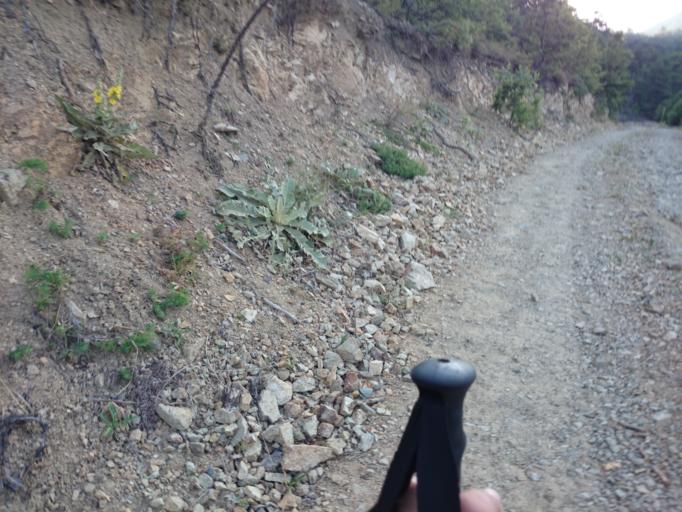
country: AL
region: Lezhe
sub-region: Rrethi i Mirdites
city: Orosh
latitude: 41.8662
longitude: 20.0808
